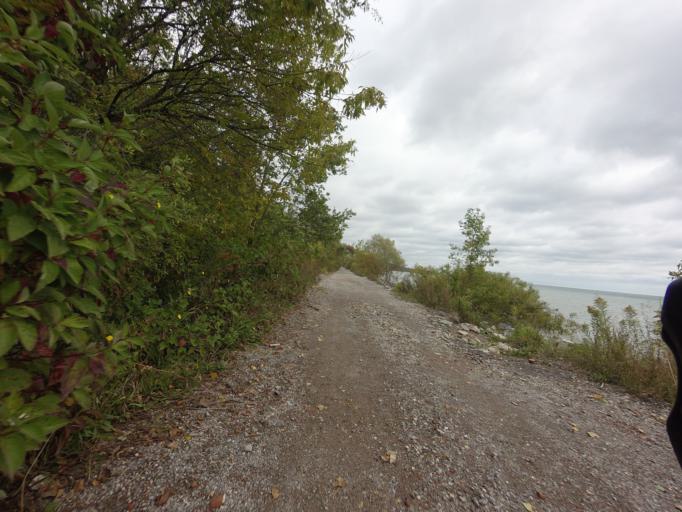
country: CA
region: Ontario
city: Scarborough
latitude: 43.7437
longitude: -79.1927
